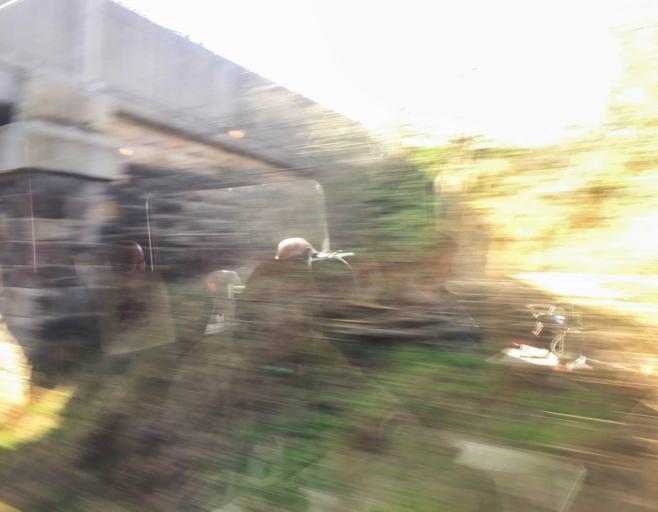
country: GB
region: Scotland
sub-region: North Lanarkshire
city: Stepps
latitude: 55.8905
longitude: -4.1316
